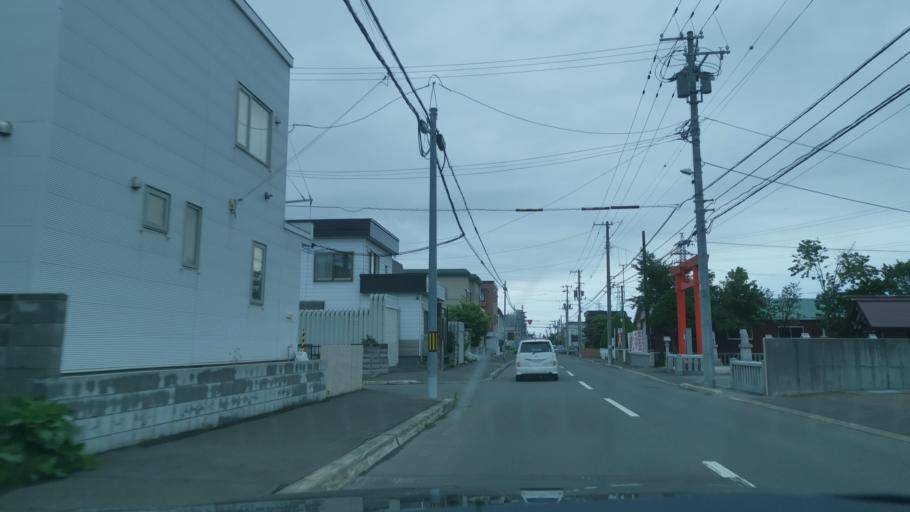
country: JP
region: Hokkaido
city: Sapporo
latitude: 43.1083
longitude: 141.3013
